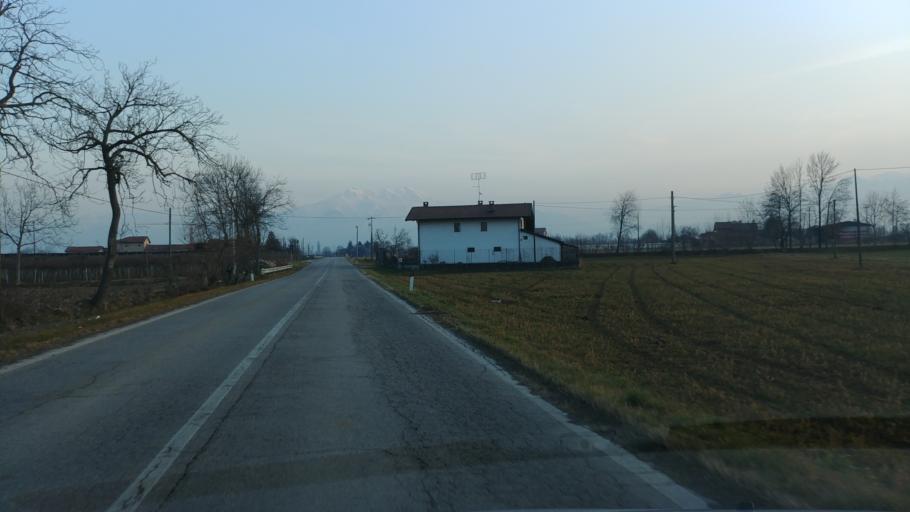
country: IT
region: Piedmont
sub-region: Provincia di Cuneo
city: Roata Rossi
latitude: 44.4185
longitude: 7.5092
